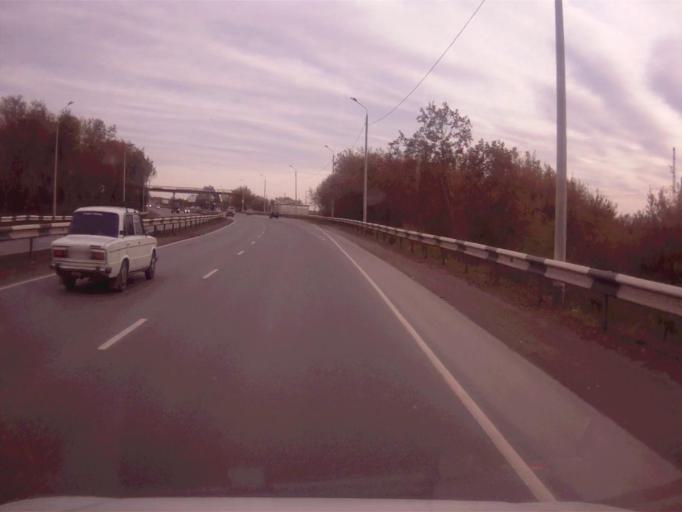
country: RU
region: Chelyabinsk
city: Novosineglazovskiy
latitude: 55.0435
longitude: 61.4243
